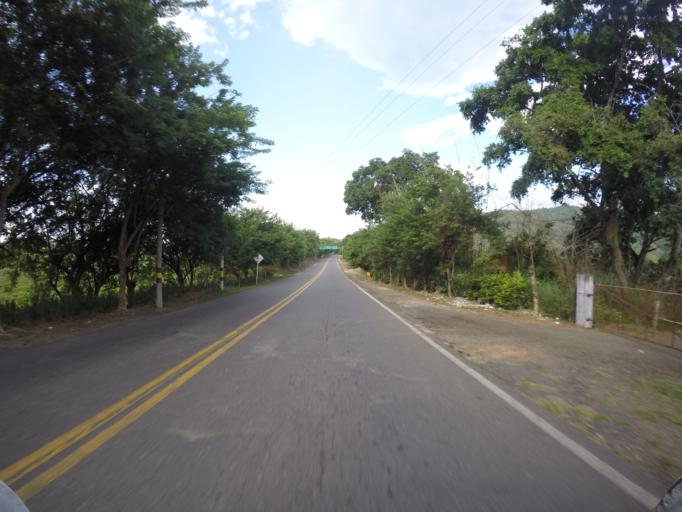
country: CO
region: Valle del Cauca
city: Cartago
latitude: 4.7251
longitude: -75.8855
